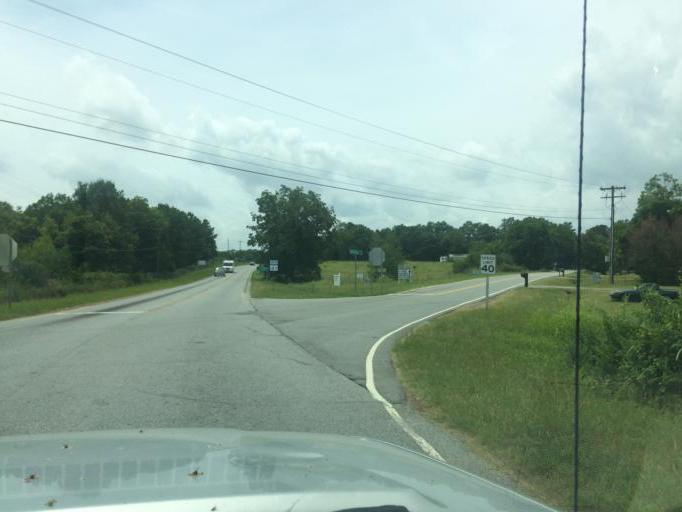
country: US
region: South Carolina
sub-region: Anderson County
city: Centerville
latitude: 34.5081
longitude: -82.7623
